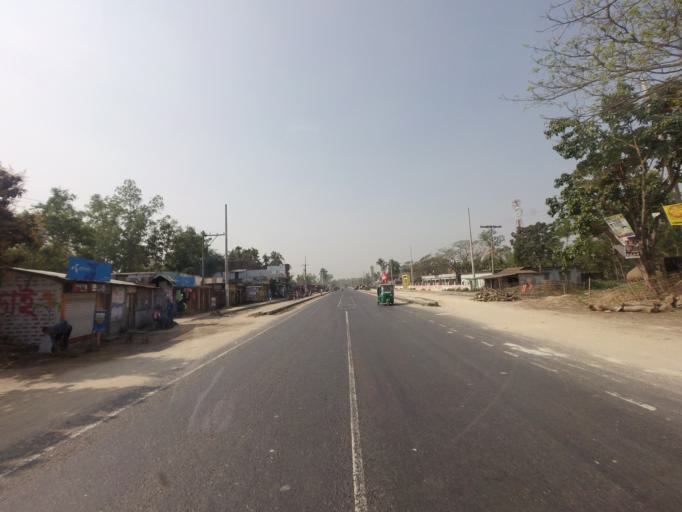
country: BD
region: Sylhet
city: Habiganj
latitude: 24.3873
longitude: 91.5550
